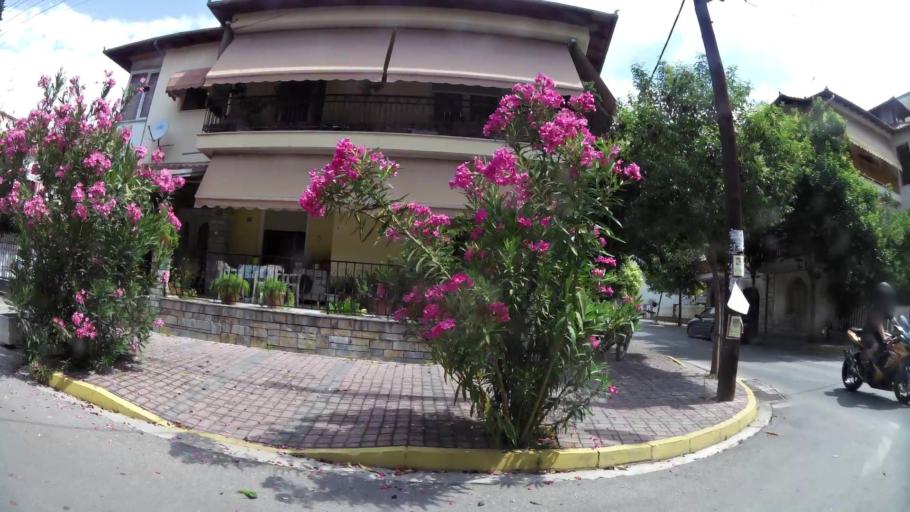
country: GR
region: Central Macedonia
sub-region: Nomos Pierias
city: Katerini
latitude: 40.2765
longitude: 22.5046
